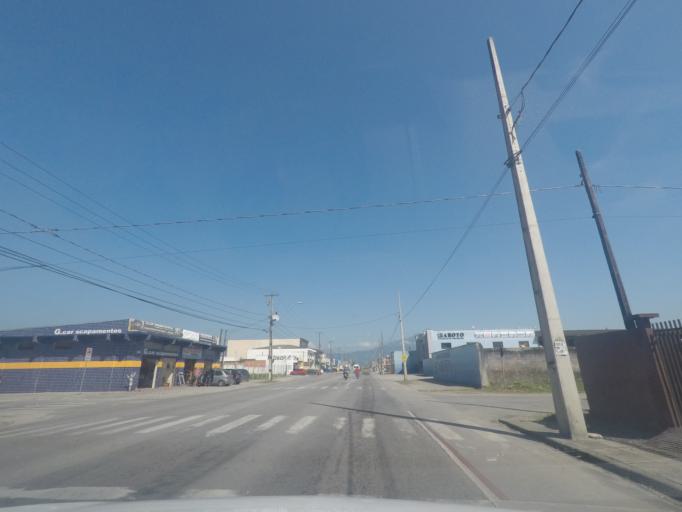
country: BR
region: Parana
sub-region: Paranagua
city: Paranagua
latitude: -25.5547
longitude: -48.5538
